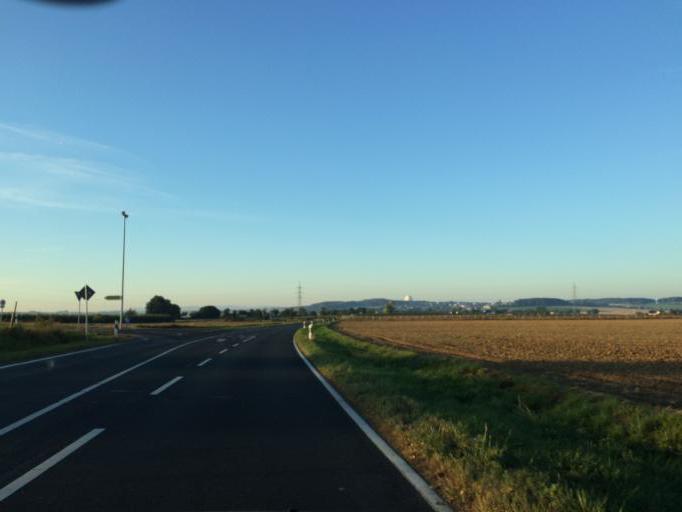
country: DE
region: North Rhine-Westphalia
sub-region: Regierungsbezirk Koln
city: Konigswinter
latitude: 50.6461
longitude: 7.1550
